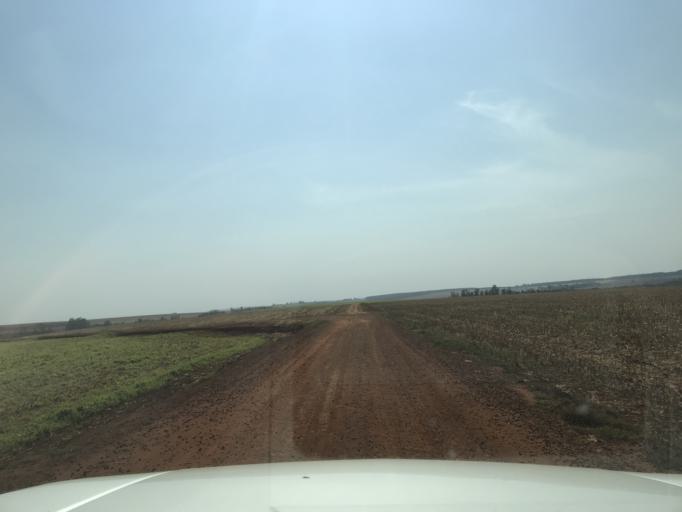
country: BR
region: Parana
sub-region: Palotina
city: Palotina
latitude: -24.2359
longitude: -53.7501
